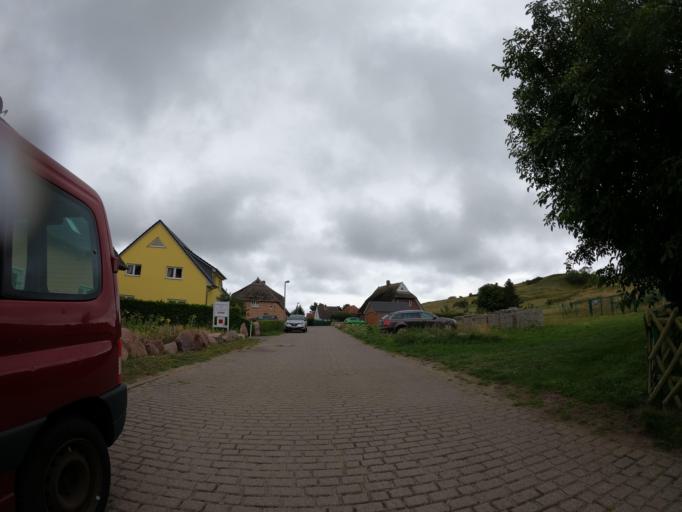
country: DE
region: Mecklenburg-Vorpommern
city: Ostseebad Gohren
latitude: 54.3073
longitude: 13.6811
